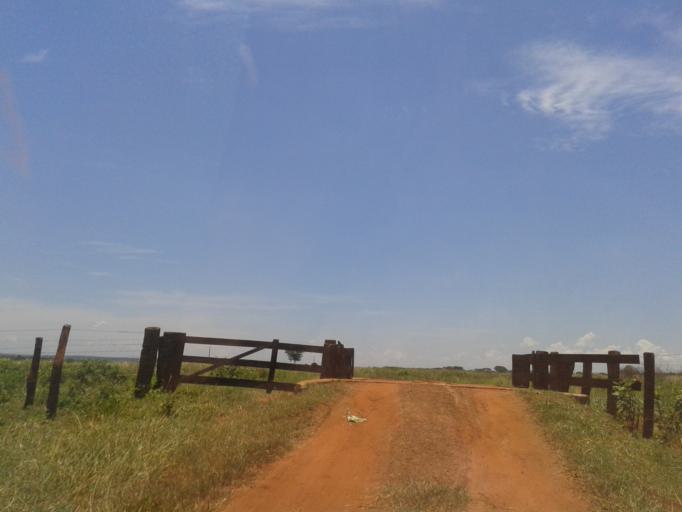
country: BR
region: Minas Gerais
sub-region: Santa Vitoria
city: Santa Vitoria
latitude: -19.2272
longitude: -50.4795
